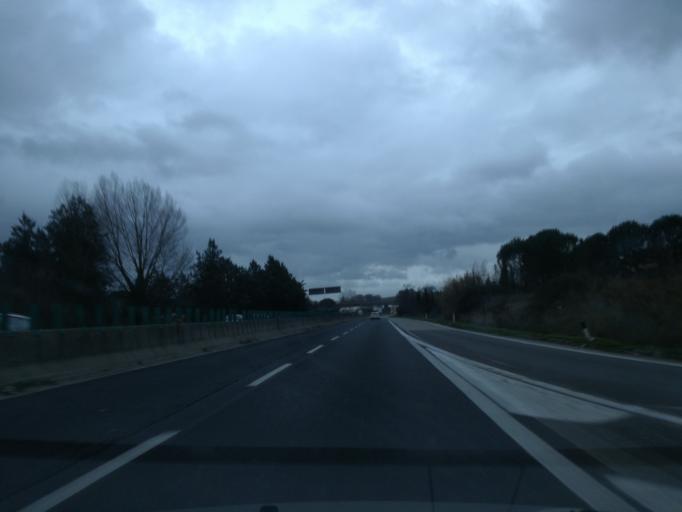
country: IT
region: Umbria
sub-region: Provincia di Perugia
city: Via Lippia
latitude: 43.1074
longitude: 12.4740
